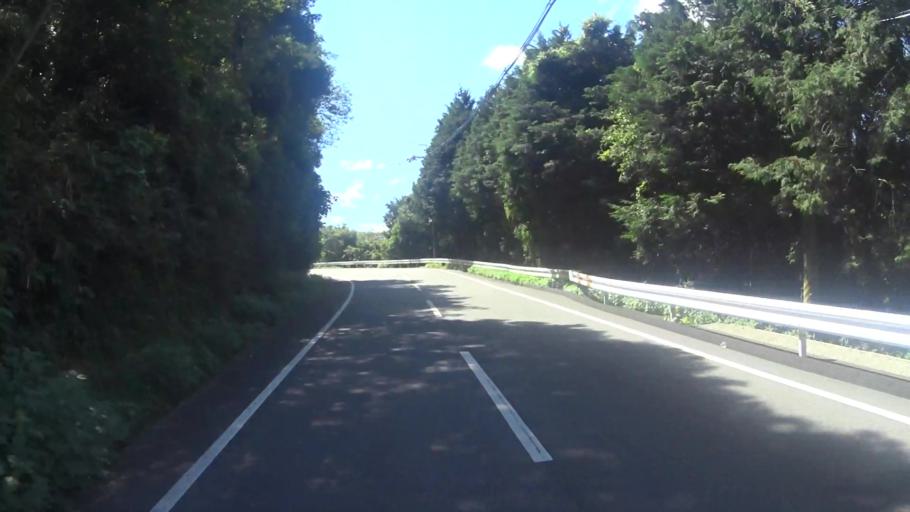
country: JP
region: Nara
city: Nara-shi
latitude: 34.7417
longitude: 135.8765
